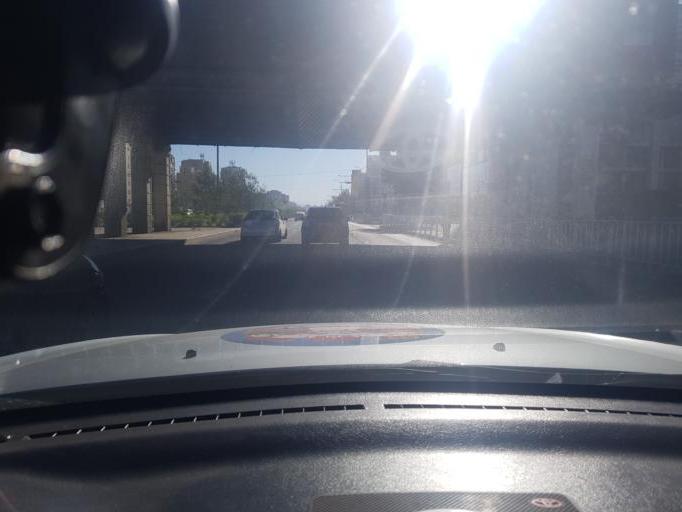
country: MN
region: Ulaanbaatar
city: Ulaanbaatar
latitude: 47.9115
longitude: 106.8373
